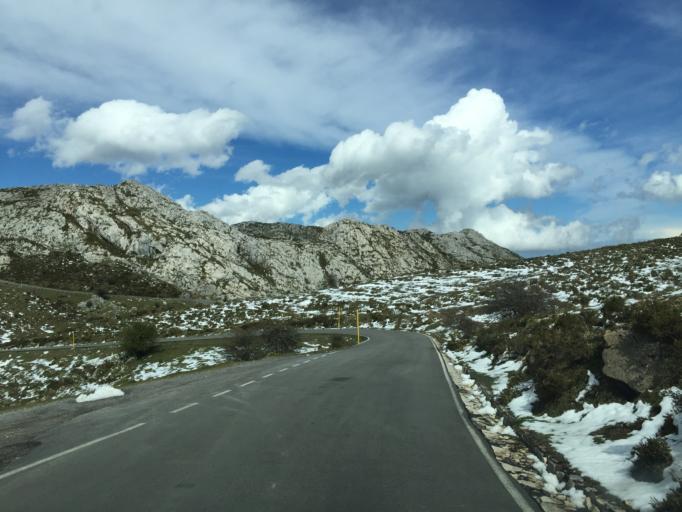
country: ES
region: Asturias
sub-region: Province of Asturias
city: Amieva
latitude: 43.2804
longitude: -5.0028
